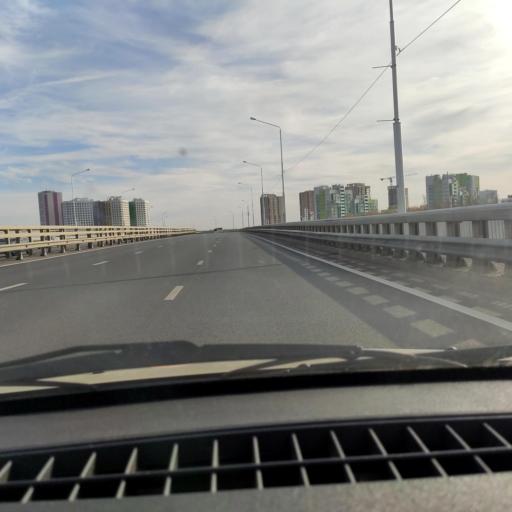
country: RU
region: Bashkortostan
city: Mikhaylovka
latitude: 54.7041
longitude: 55.8574
